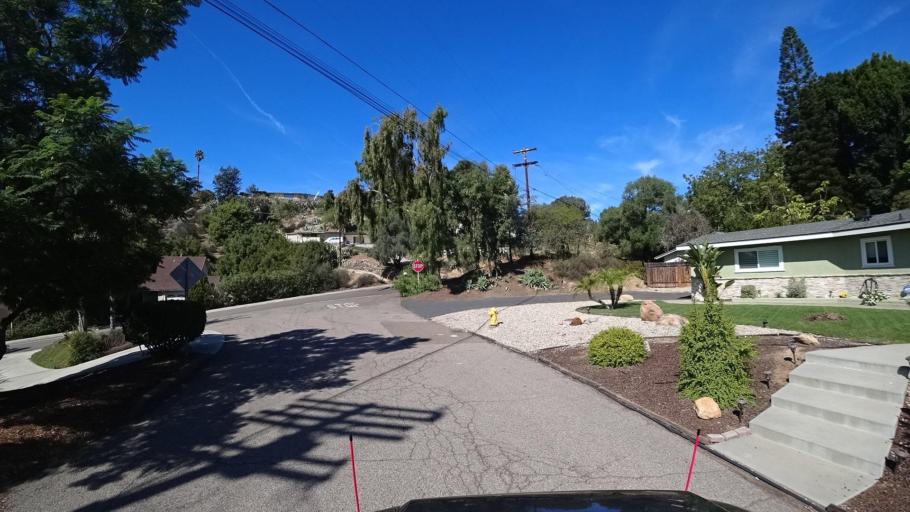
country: US
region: California
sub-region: San Diego County
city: Casa de Oro-Mount Helix
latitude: 32.7548
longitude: -116.9726
